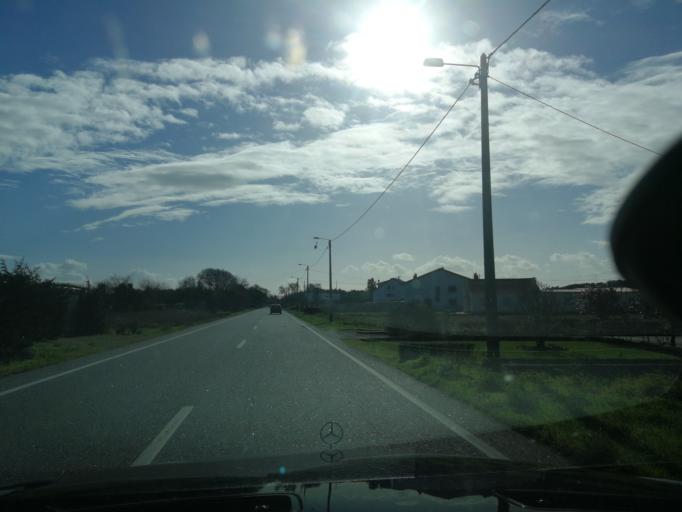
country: PT
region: Aveiro
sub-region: Estarreja
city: Pardilho
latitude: 40.8228
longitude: -8.6681
